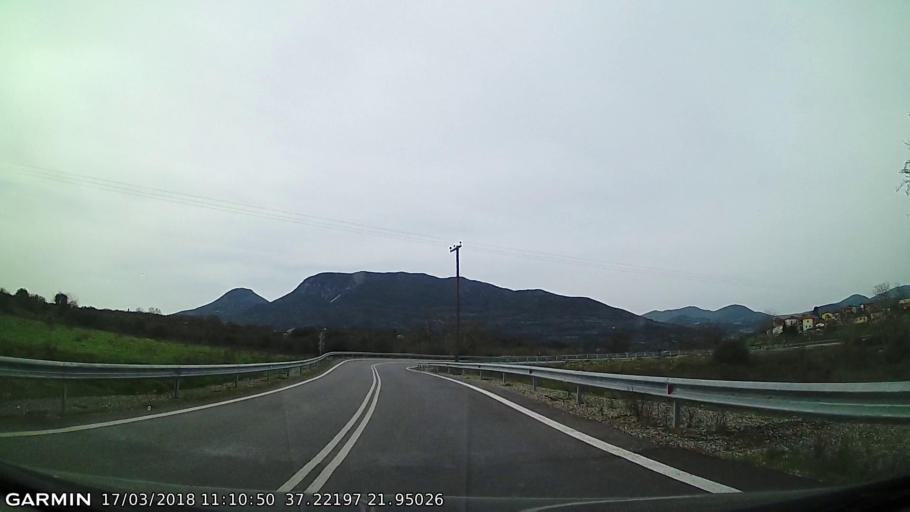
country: GR
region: Peloponnese
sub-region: Nomos Messinias
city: Meligalas
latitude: 37.2220
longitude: 21.9502
